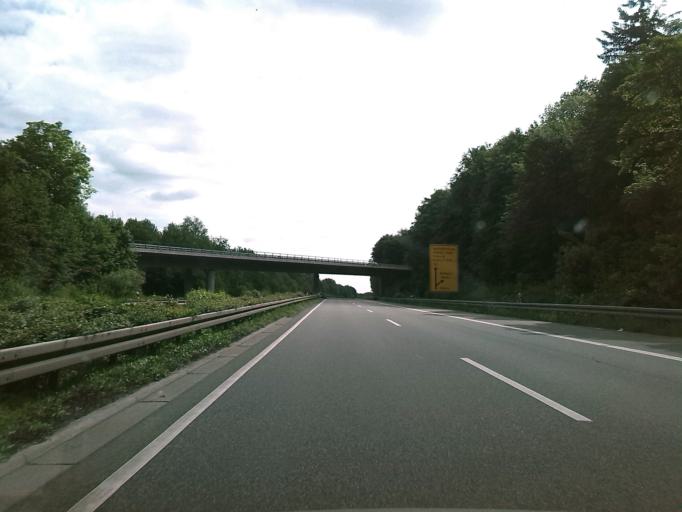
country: DE
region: Hesse
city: Ober-Ramstadt
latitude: 49.8652
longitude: 8.7069
